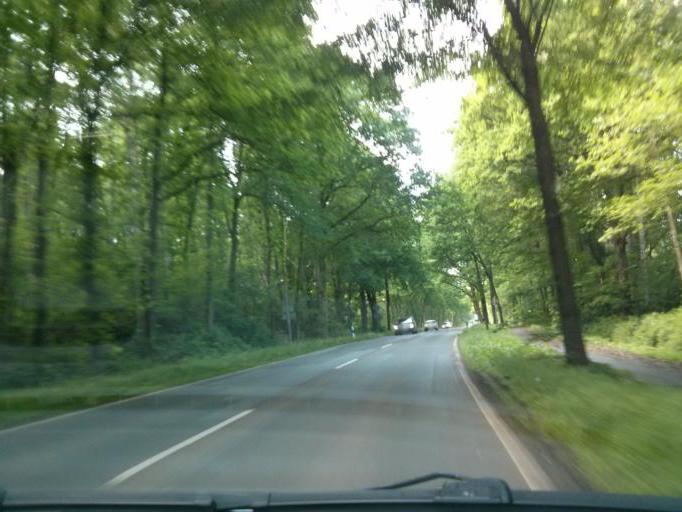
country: DE
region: Lower Saxony
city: Schiffdorf
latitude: 53.5169
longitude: 8.6787
